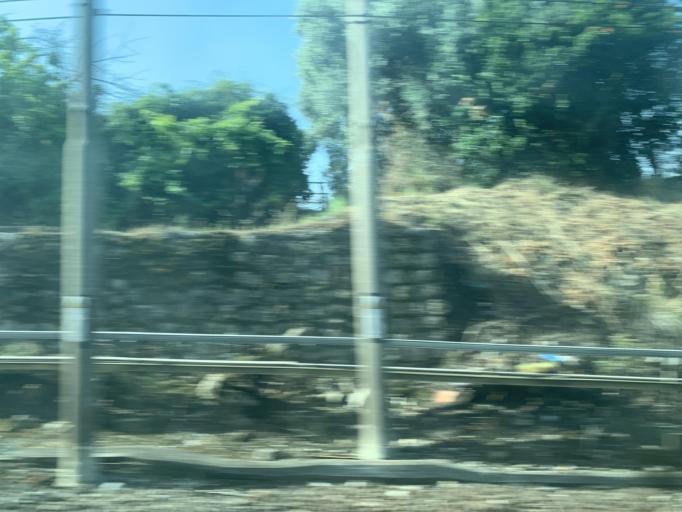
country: IT
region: Latium
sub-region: Provincia di Latina
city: Gaeta
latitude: 41.2546
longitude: 13.5895
